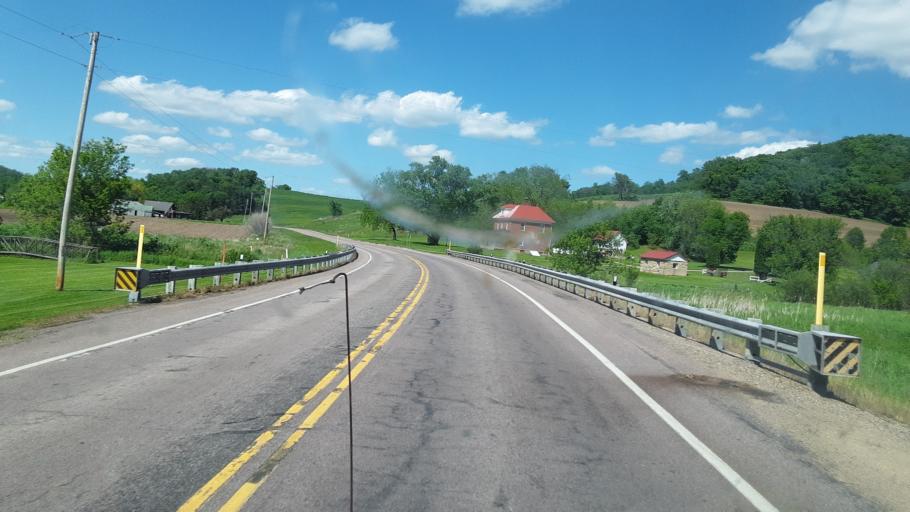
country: US
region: Wisconsin
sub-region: Richland County
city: Richland Center
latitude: 43.3593
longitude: -90.2674
